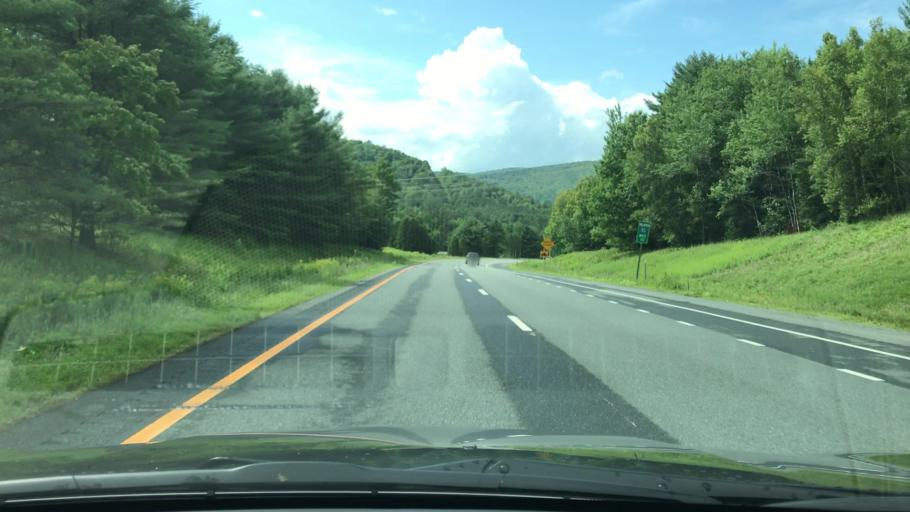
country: US
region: New Hampshire
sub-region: Grafton County
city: Littleton
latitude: 44.3339
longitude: -71.8837
